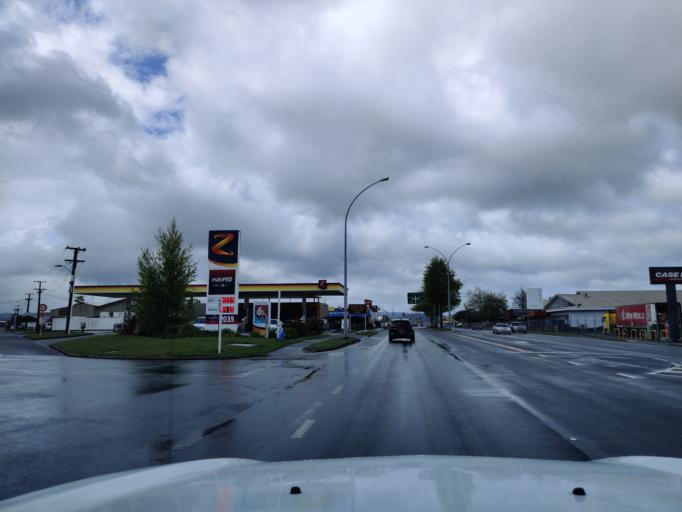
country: NZ
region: Bay of Plenty
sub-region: Rotorua District
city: Rotorua
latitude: -38.1225
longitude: 176.2300
